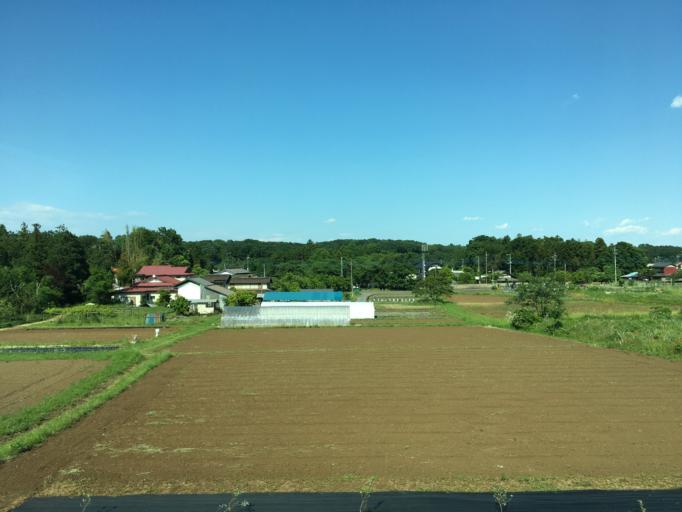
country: JP
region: Saitama
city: Morohongo
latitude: 35.9788
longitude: 139.3350
